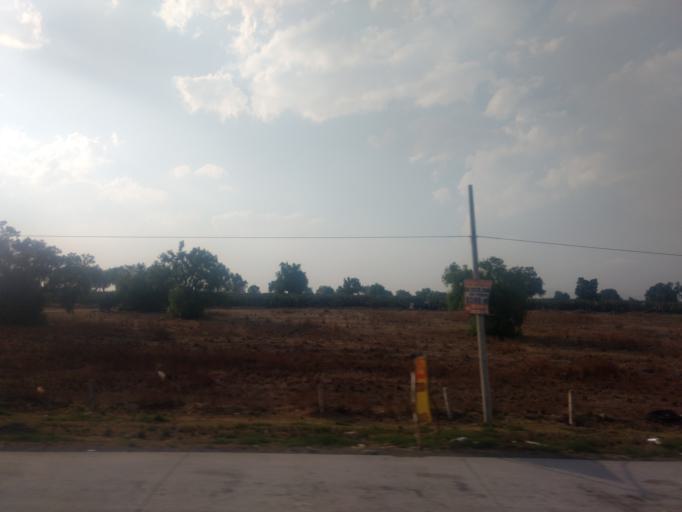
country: MX
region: Morelos
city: Nopaltepec
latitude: 19.8317
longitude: -98.7024
